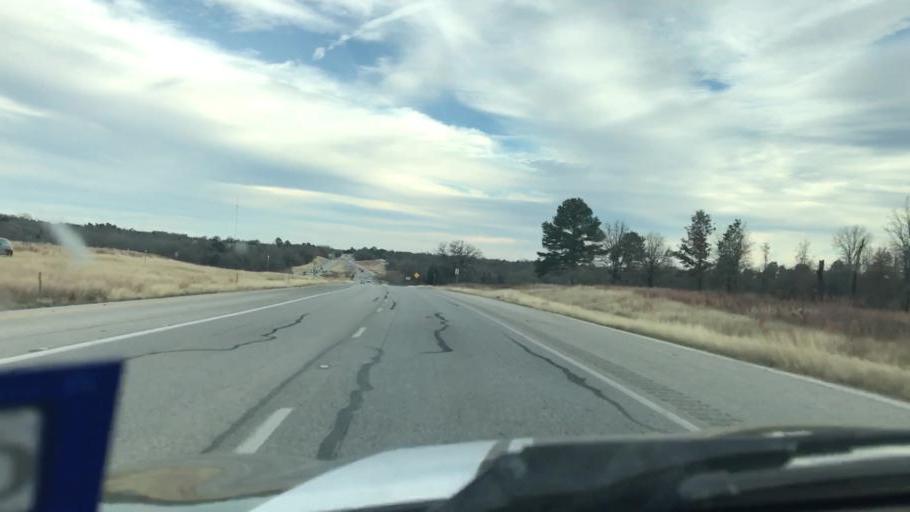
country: US
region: Texas
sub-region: Bastrop County
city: Elgin
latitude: 30.3071
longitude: -97.3013
